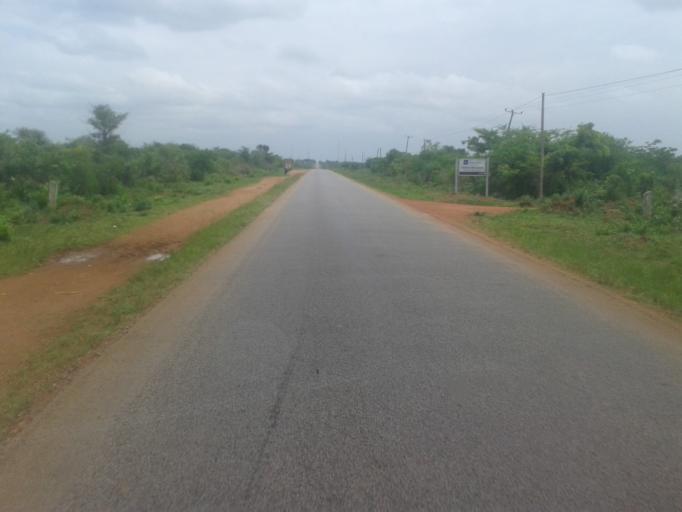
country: UG
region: Western Region
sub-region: Kiryandongo District
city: Masindi Port
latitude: 1.5005
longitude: 32.1236
